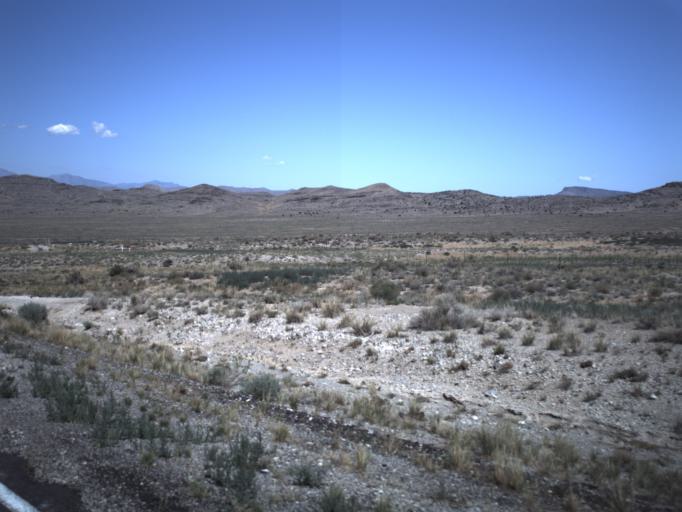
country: US
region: Utah
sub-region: Beaver County
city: Milford
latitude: 39.0725
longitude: -113.6629
